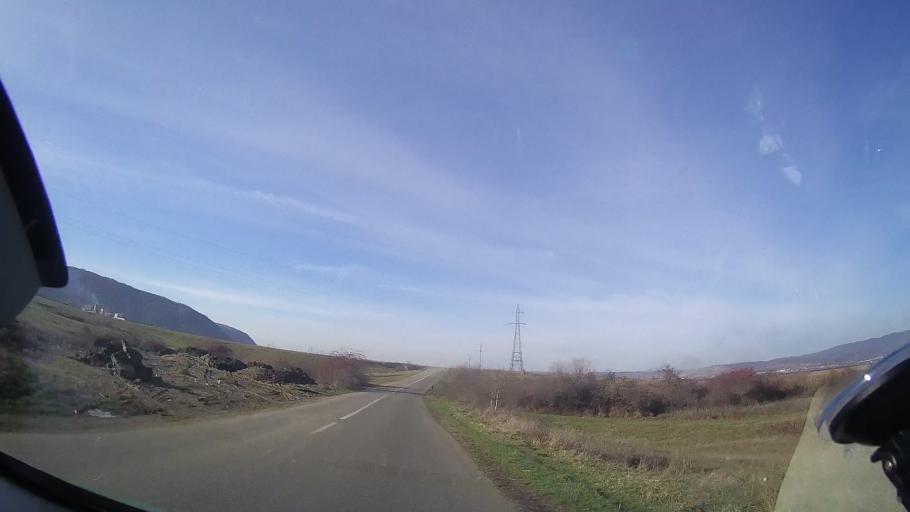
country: RO
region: Bihor
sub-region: Comuna Magesti
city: Magesti
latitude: 47.0204
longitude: 22.4209
